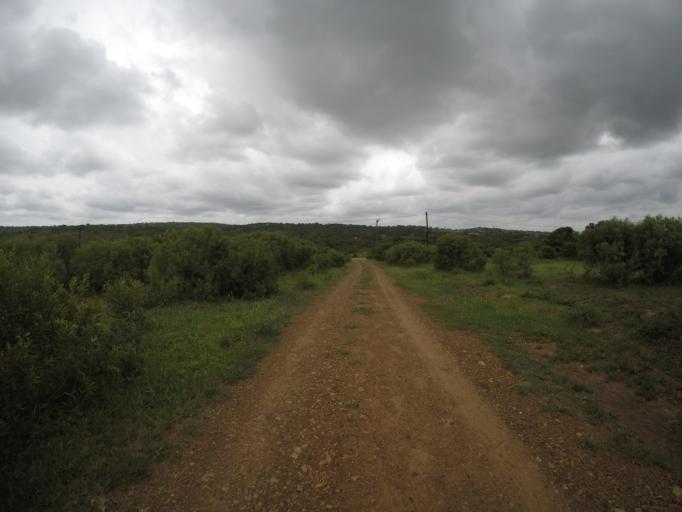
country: ZA
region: KwaZulu-Natal
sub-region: uThungulu District Municipality
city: Empangeni
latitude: -28.5949
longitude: 31.8332
